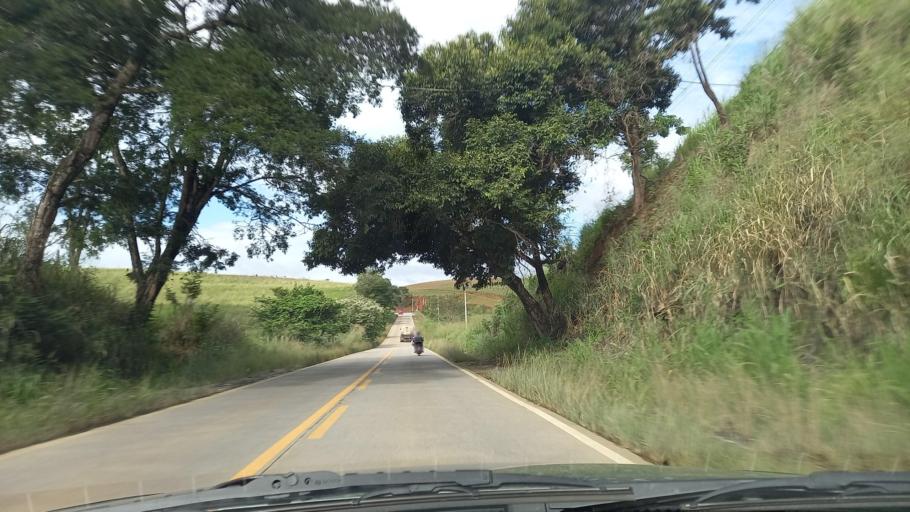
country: BR
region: Pernambuco
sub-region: Maraial
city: Maraial
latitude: -8.7494
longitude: -35.8120
